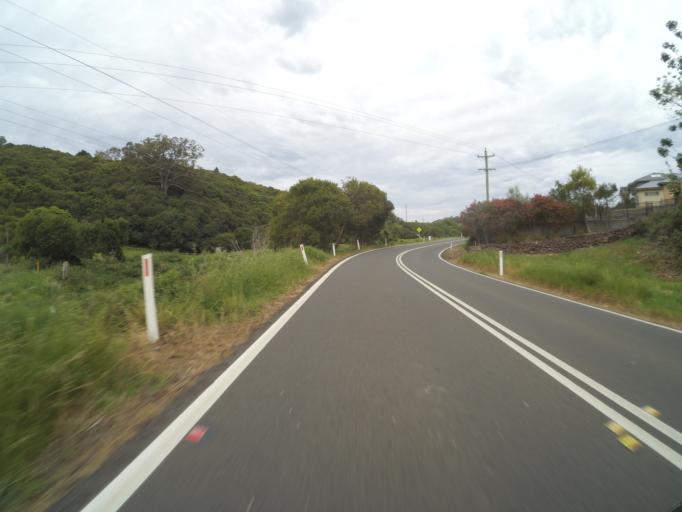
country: AU
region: New South Wales
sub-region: Kiama
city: Kiama
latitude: -34.6624
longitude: 150.8400
